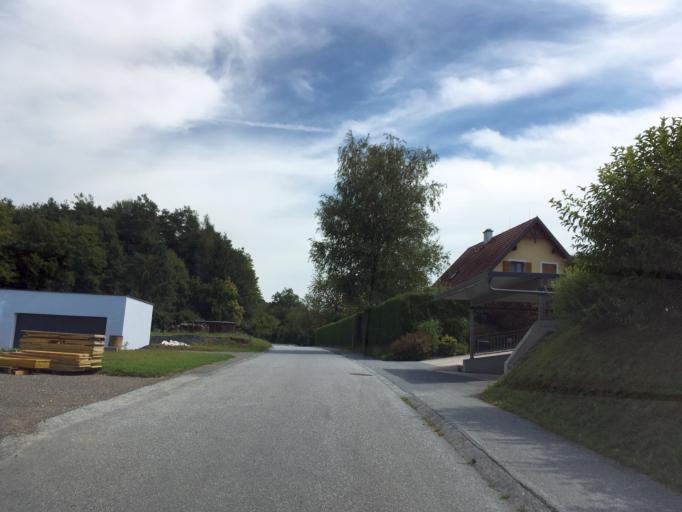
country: AT
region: Styria
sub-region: Politischer Bezirk Leibnitz
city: Pistorf
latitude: 46.7901
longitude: 15.3822
